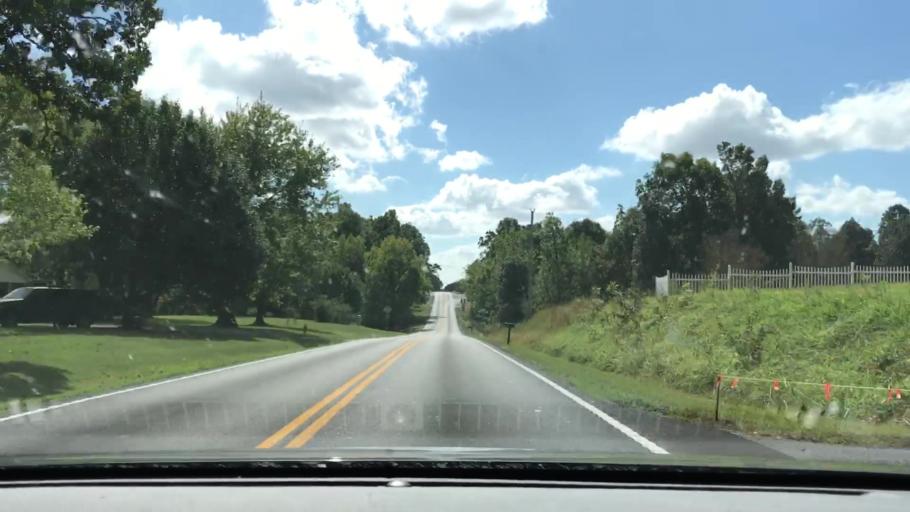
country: US
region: Kentucky
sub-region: Graves County
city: Mayfield
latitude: 36.7799
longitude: -88.5959
